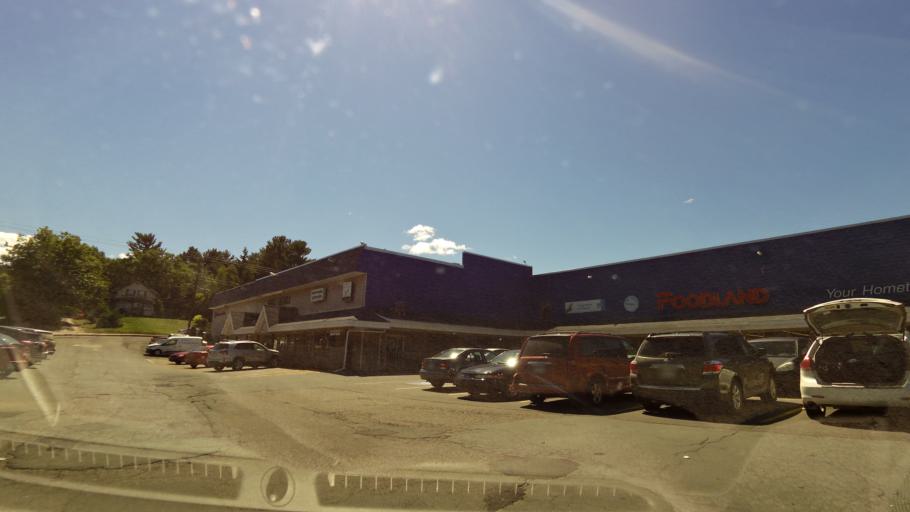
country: CA
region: Nova Scotia
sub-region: Kings County
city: Kentville
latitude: 45.0623
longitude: -64.5993
